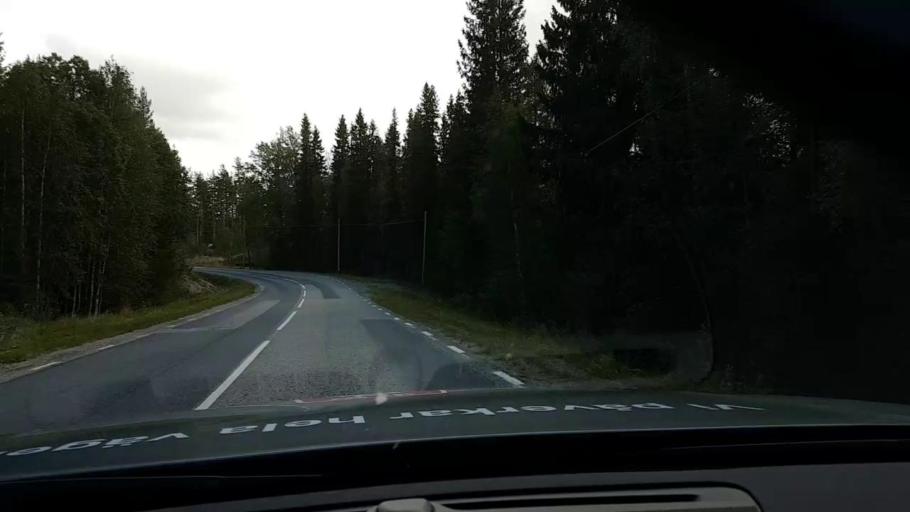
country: SE
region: Vaesterbotten
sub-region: Asele Kommun
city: Asele
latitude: 63.7953
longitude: 17.5667
